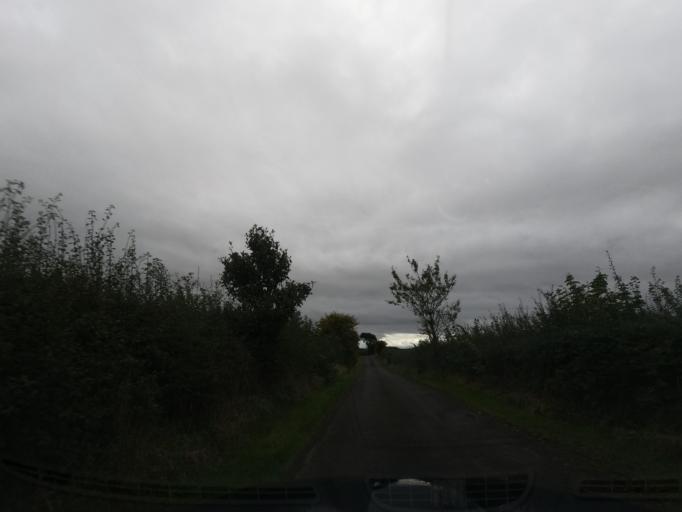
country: GB
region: England
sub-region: Northumberland
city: Ford
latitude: 55.7025
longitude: -2.0862
